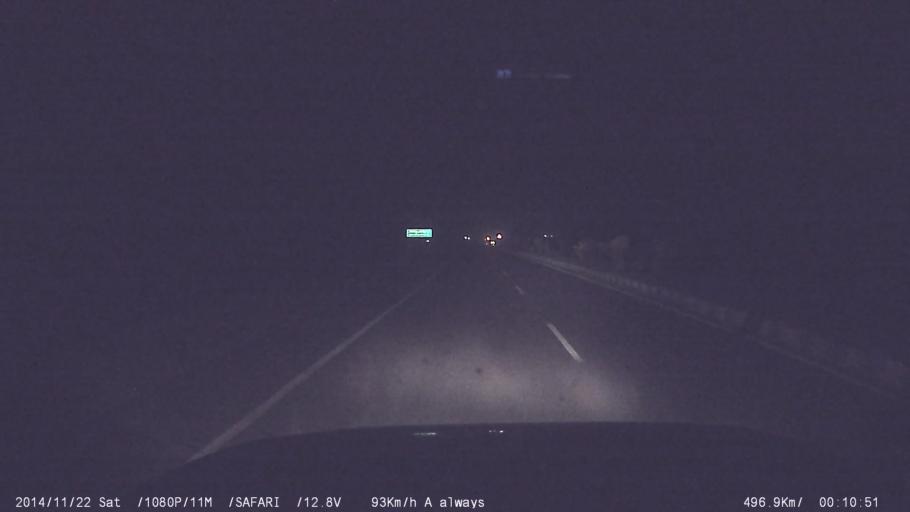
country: IN
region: Tamil Nadu
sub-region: Villupuram
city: Kallakkurichchi
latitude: 11.7349
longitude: 79.0363
